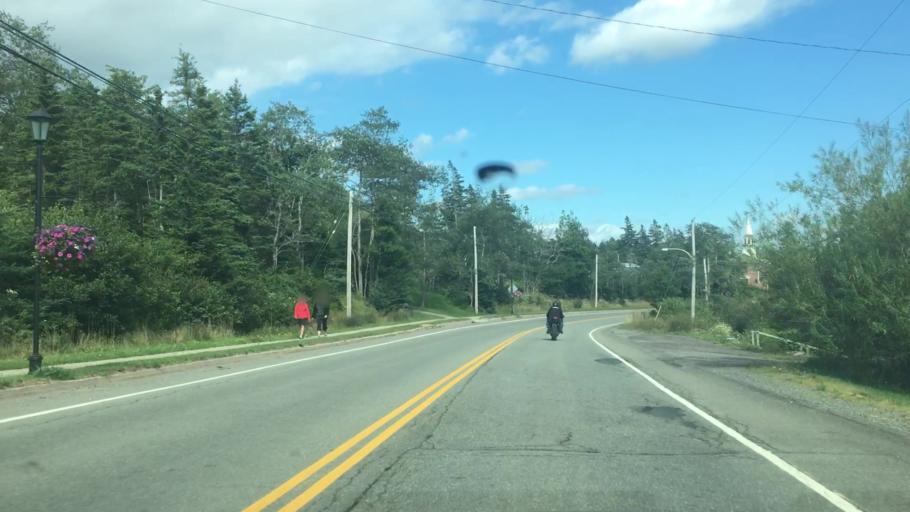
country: CA
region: Nova Scotia
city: Princeville
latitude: 45.6554
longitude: -60.8877
